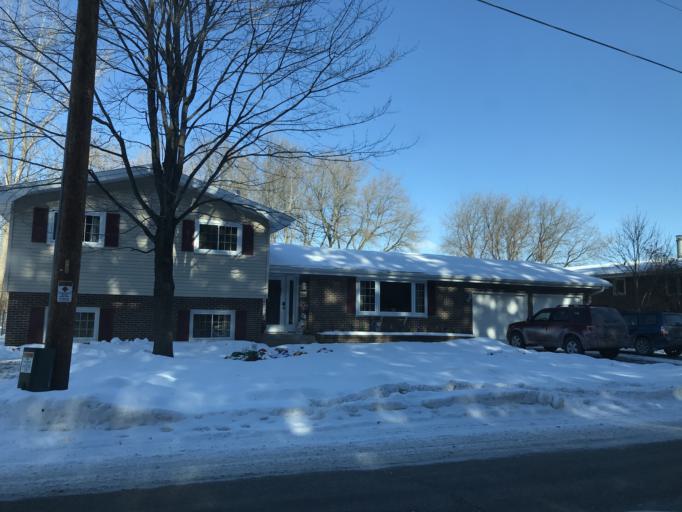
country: US
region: Wisconsin
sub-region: Marinette County
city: Marinette
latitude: 45.0781
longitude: -87.6252
